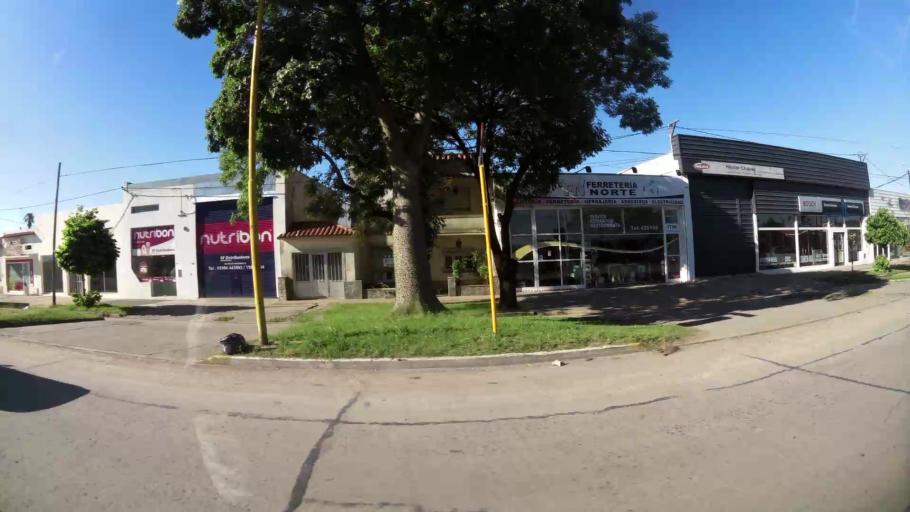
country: AR
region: Cordoba
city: San Francisco
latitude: -31.4167
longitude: -62.0828
